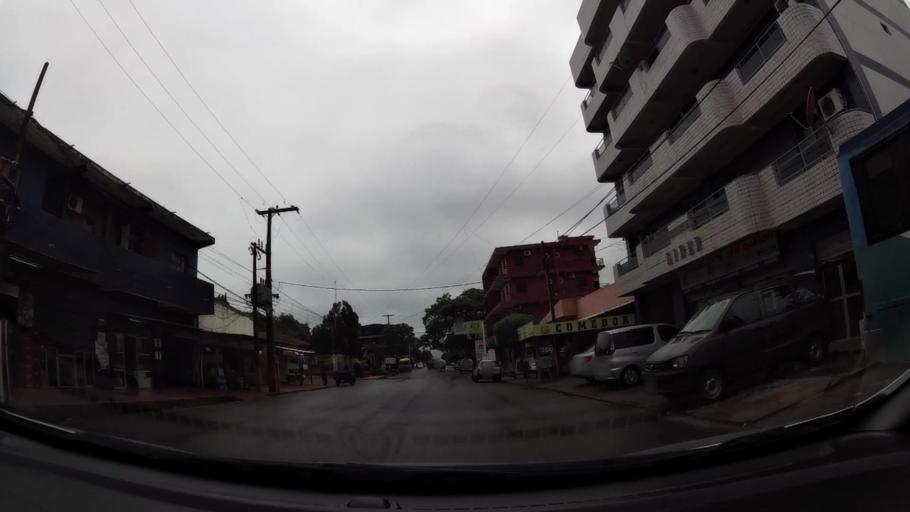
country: PY
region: Alto Parana
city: Ciudad del Este
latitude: -25.5081
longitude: -54.6608
